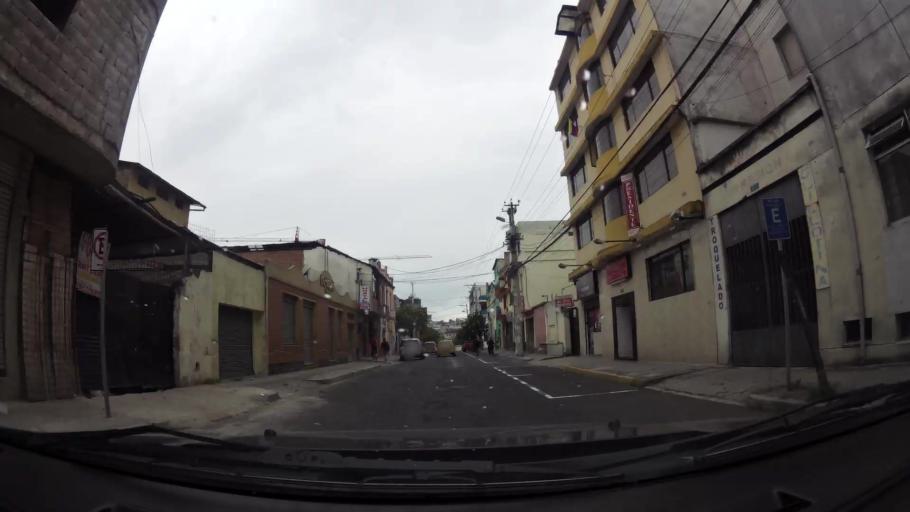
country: EC
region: Pichincha
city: Quito
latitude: -0.2066
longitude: -78.5020
